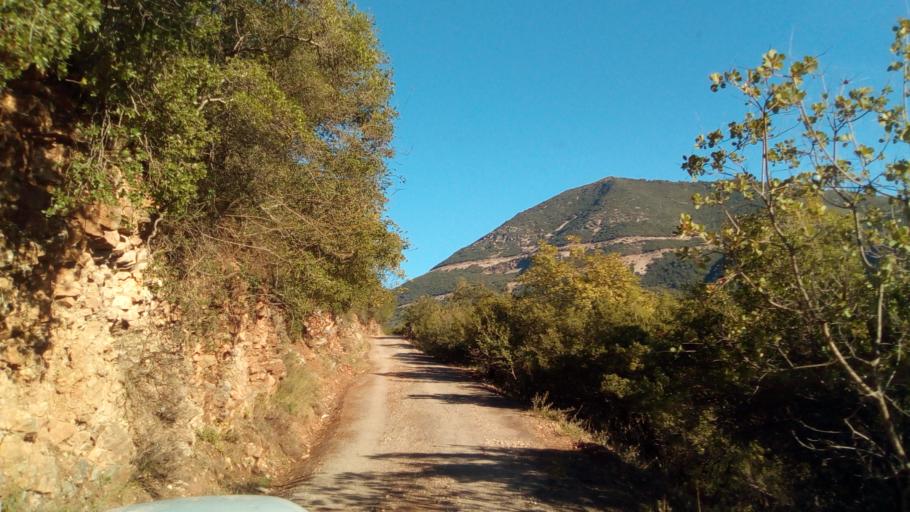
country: GR
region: West Greece
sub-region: Nomos Aitolias kai Akarnanias
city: Nafpaktos
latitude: 38.4667
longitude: 21.8675
